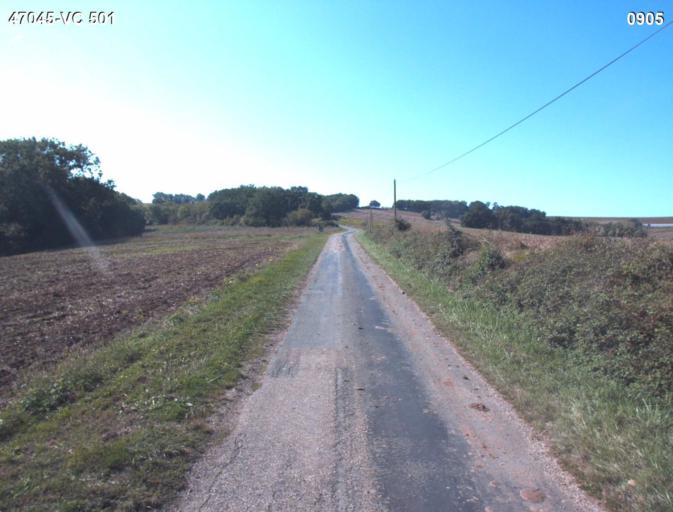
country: FR
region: Aquitaine
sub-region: Departement du Lot-et-Garonne
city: Nerac
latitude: 44.1587
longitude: 0.4083
